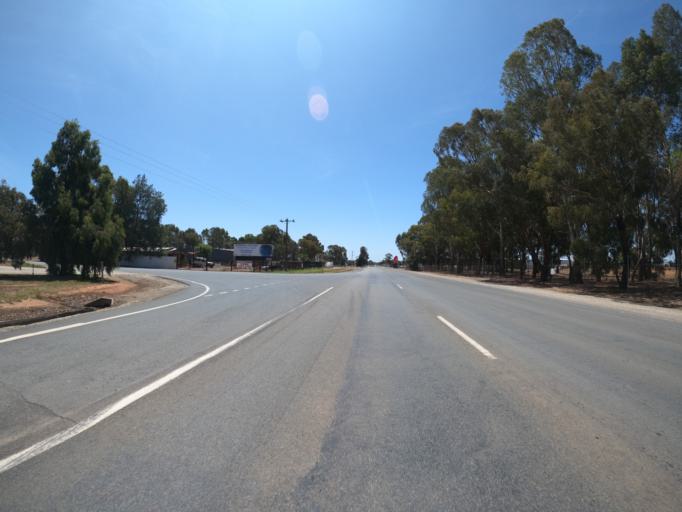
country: AU
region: Victoria
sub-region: Moira
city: Yarrawonga
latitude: -36.0326
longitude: 145.9955
